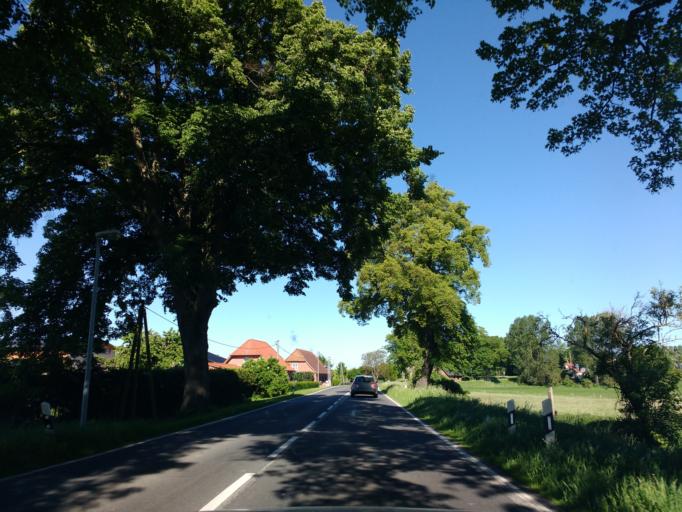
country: DE
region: Mecklenburg-Vorpommern
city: Zurow
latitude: 53.8482
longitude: 11.6362
